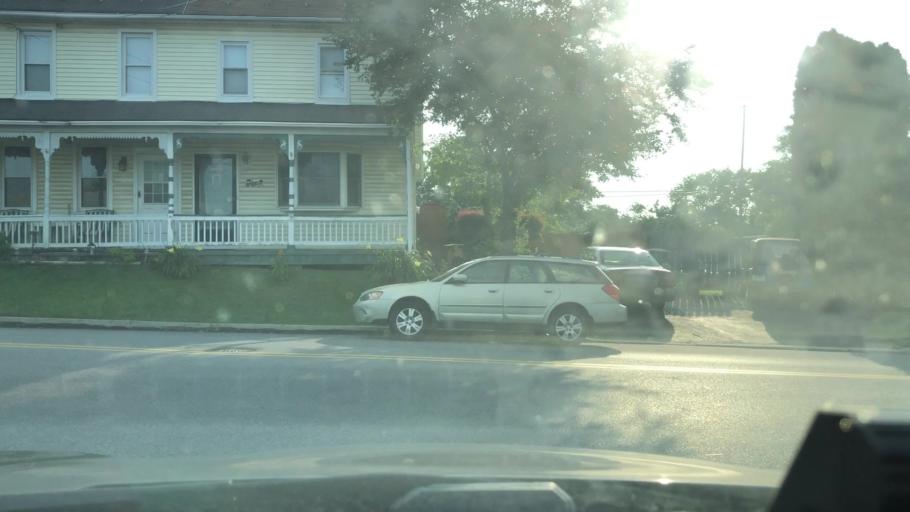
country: US
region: Pennsylvania
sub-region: Lehigh County
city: Fullerton
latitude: 40.6266
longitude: -75.4442
